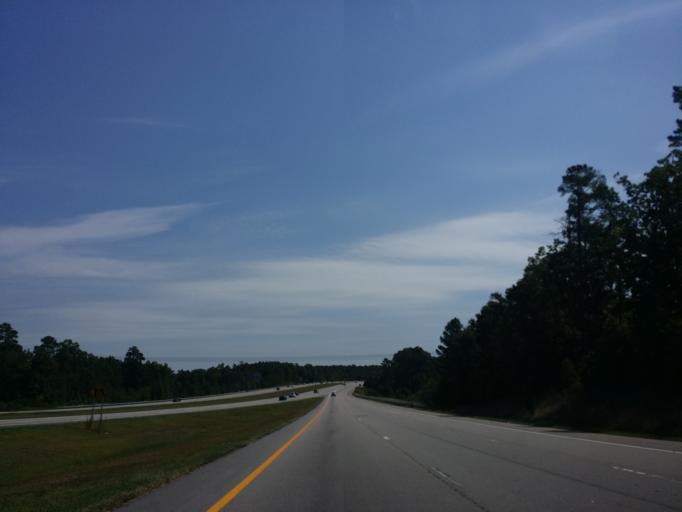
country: US
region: North Carolina
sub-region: Wake County
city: Morrisville
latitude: 35.9070
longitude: -78.7657
